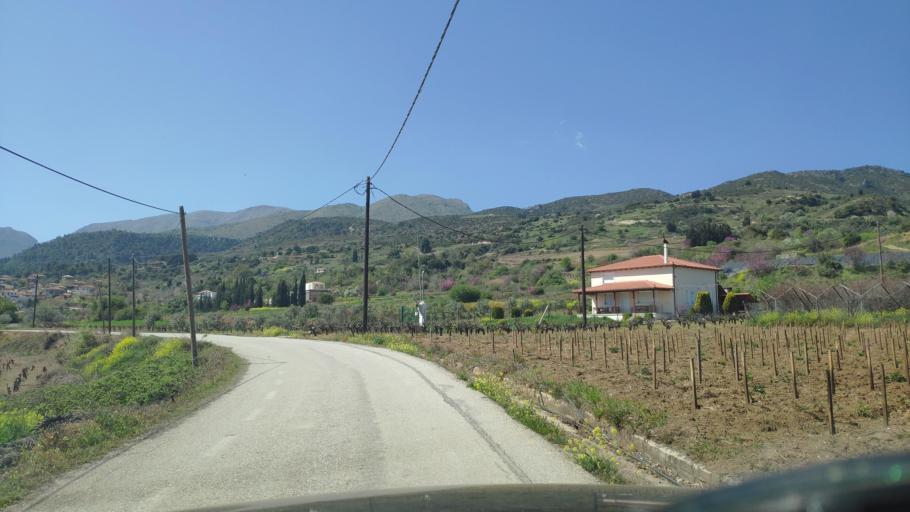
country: GR
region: West Greece
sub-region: Nomos Achaias
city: Akrata
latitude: 38.1076
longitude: 22.3172
